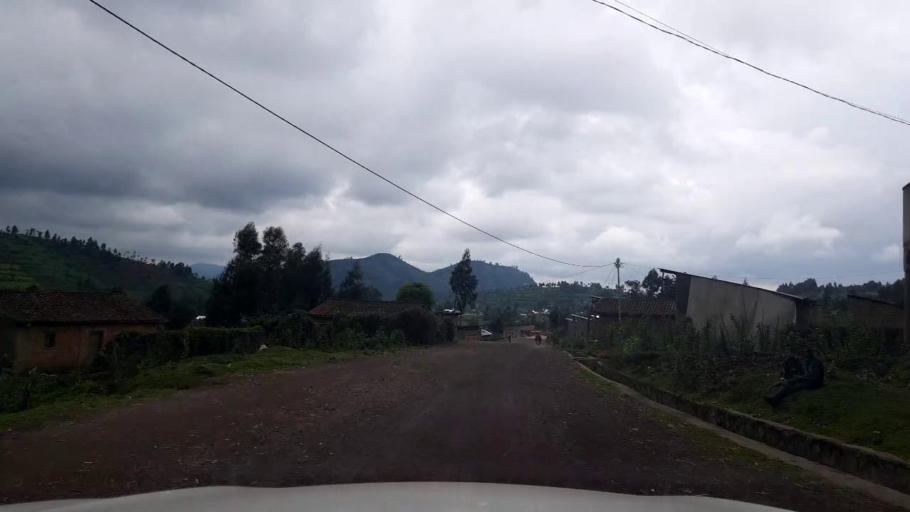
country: RW
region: Northern Province
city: Musanze
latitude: -1.5757
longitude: 29.4896
